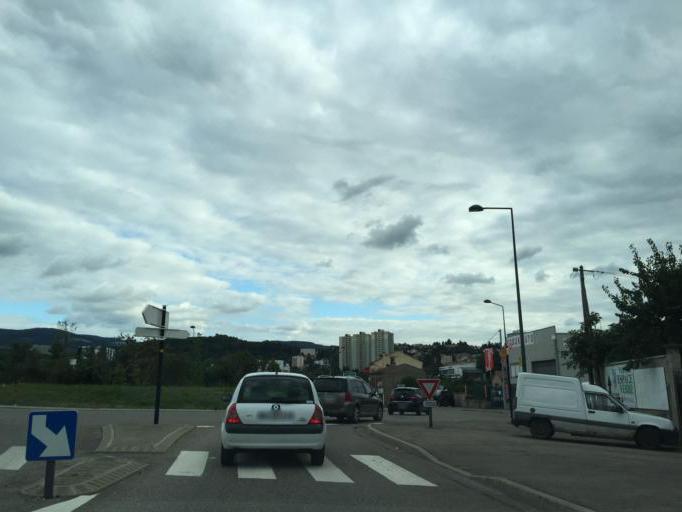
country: FR
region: Rhone-Alpes
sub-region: Departement de la Loire
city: Saint-Etienne
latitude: 45.4496
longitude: 4.4156
